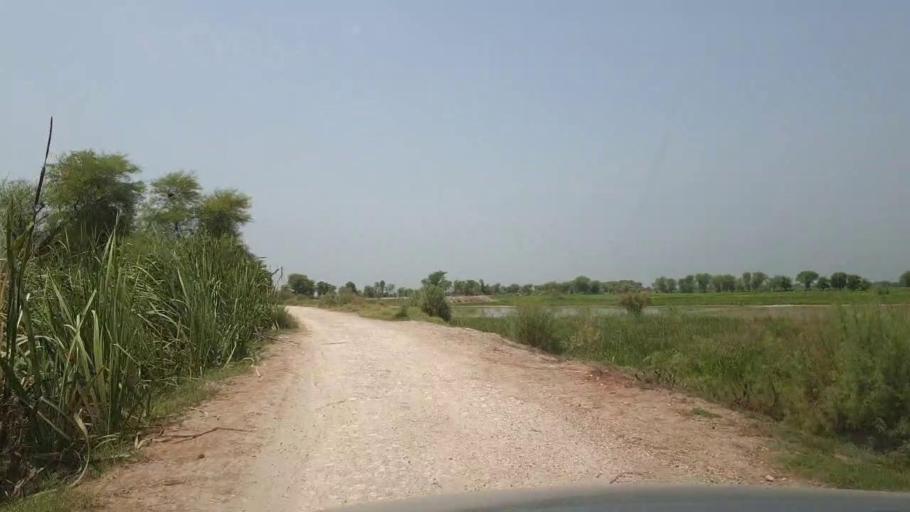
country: PK
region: Sindh
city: Garhi Yasin
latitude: 27.8373
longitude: 68.4980
